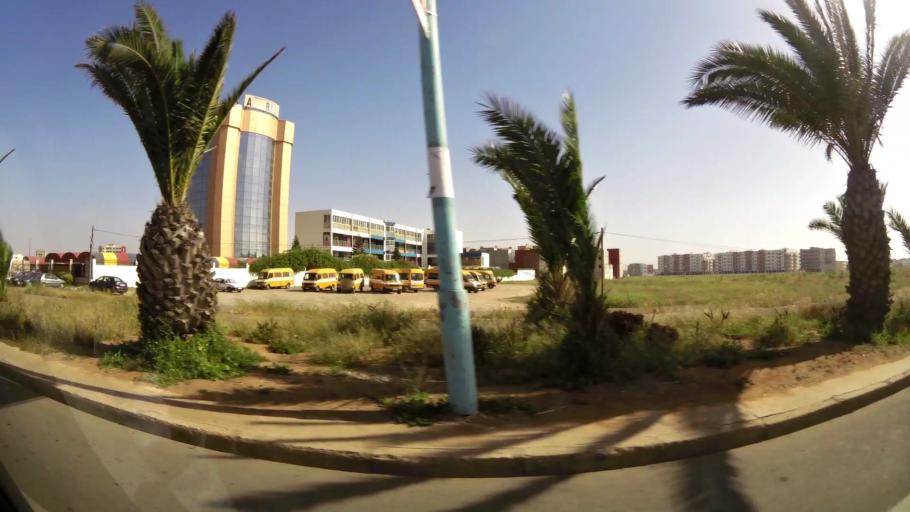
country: MA
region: Oued ed Dahab-Lagouira
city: Dakhla
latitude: 30.4038
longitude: -9.5682
